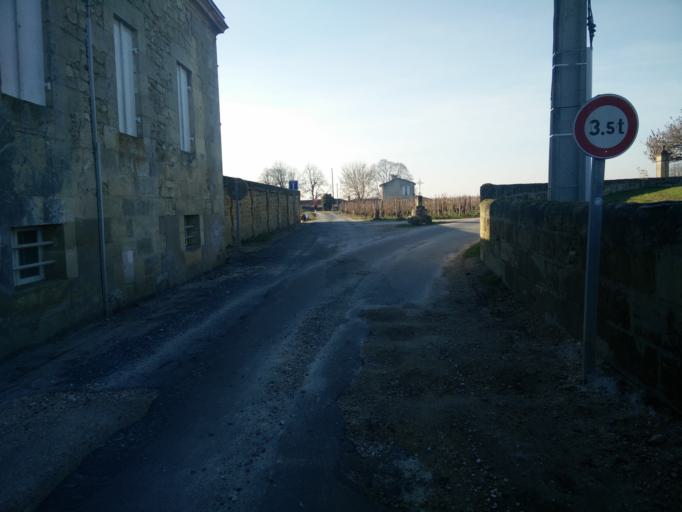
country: FR
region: Aquitaine
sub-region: Departement de la Gironde
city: Saint-Emilion
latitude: 44.8890
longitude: -0.1628
